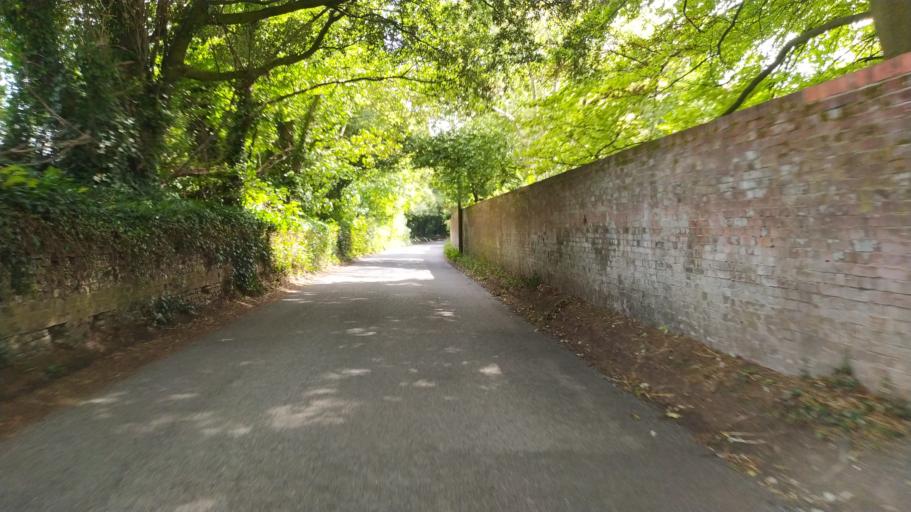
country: GB
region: England
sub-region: Dorset
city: Blandford Forum
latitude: 50.8495
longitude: -2.1385
